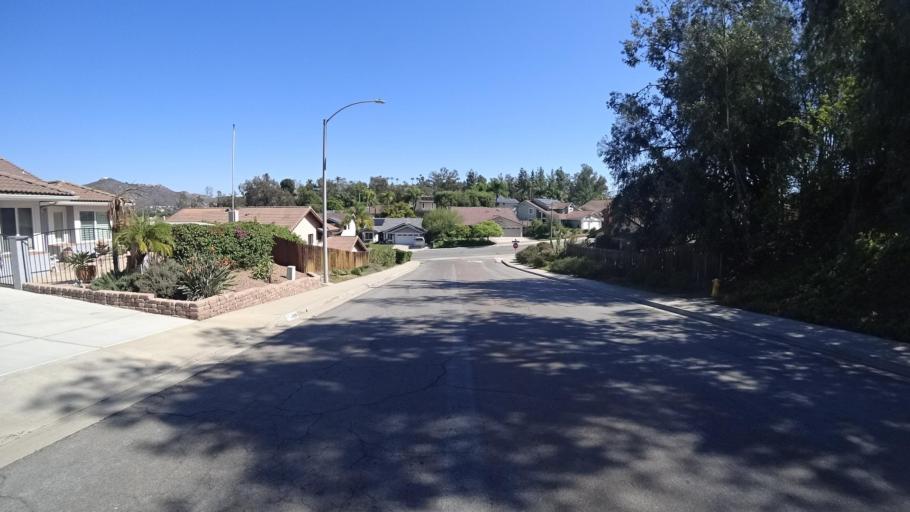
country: US
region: California
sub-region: San Diego County
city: Rancho San Diego
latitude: 32.7526
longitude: -116.9188
